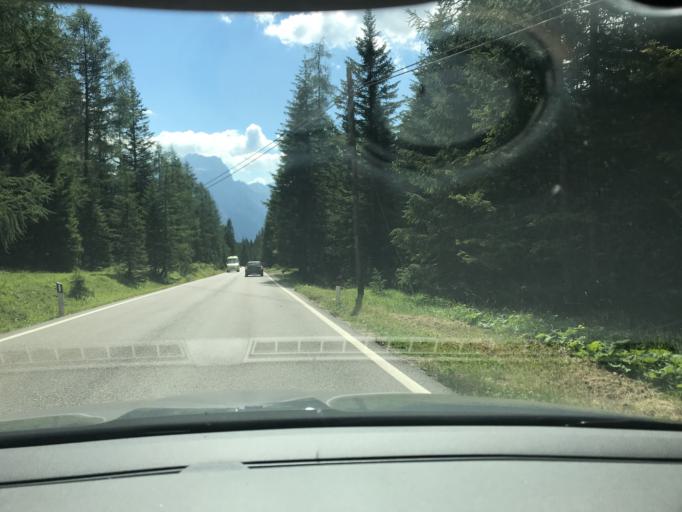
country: IT
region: Veneto
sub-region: Provincia di Belluno
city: Selva di Cadore
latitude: 46.5230
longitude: 12.0580
